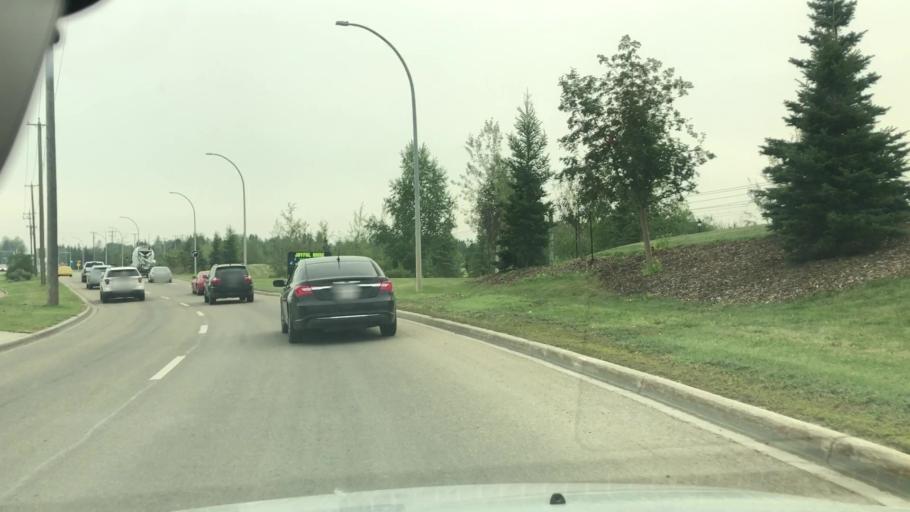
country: CA
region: Alberta
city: Edmonton
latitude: 53.4982
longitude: -113.5215
